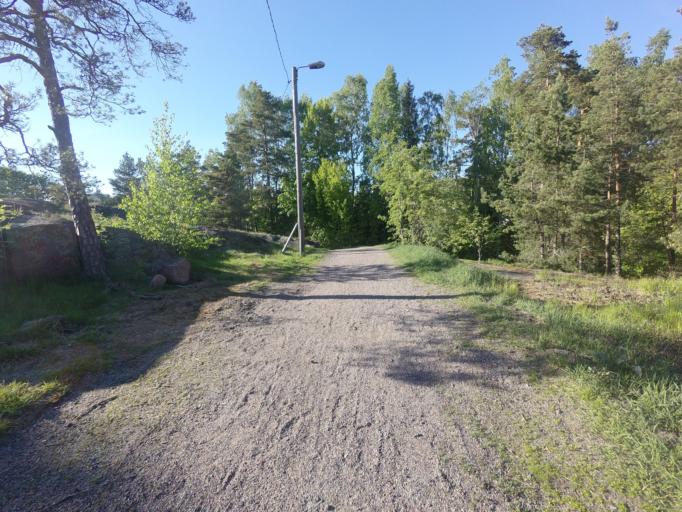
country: FI
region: Uusimaa
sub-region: Helsinki
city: Koukkuniemi
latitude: 60.1721
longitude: 24.7416
